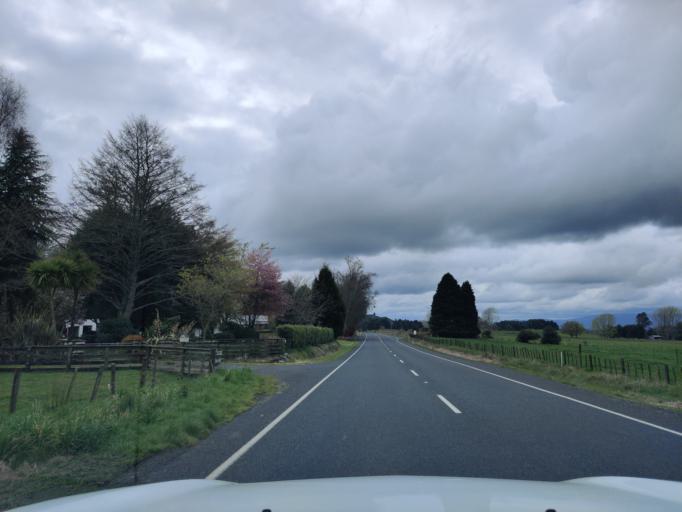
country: NZ
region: Waikato
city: Turangi
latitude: -38.9900
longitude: 175.3786
